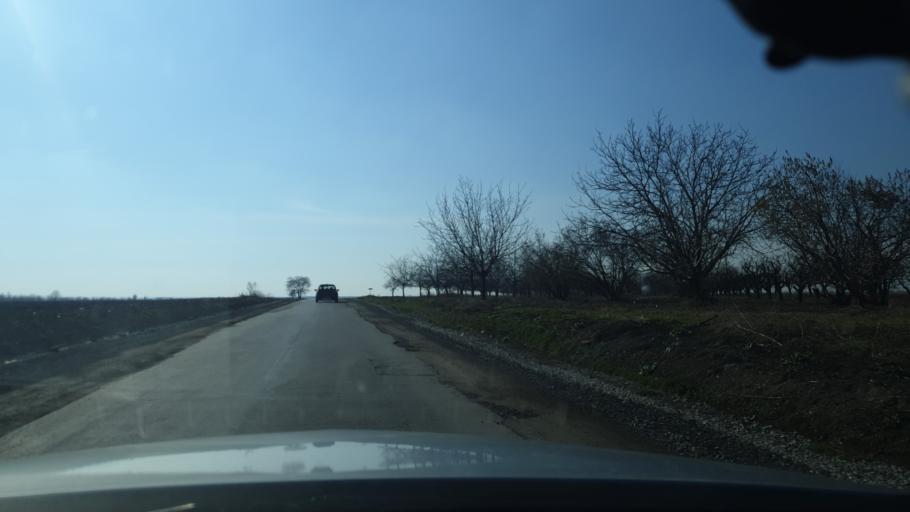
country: RS
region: Autonomna Pokrajina Vojvodina
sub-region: Sremski Okrug
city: Irig
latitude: 45.0822
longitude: 19.8470
